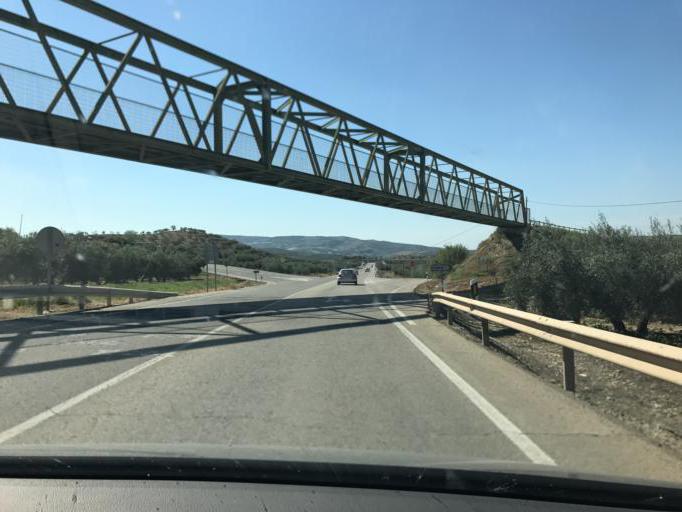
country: ES
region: Andalusia
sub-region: Province of Cordoba
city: Luque
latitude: 37.5736
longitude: -4.2646
